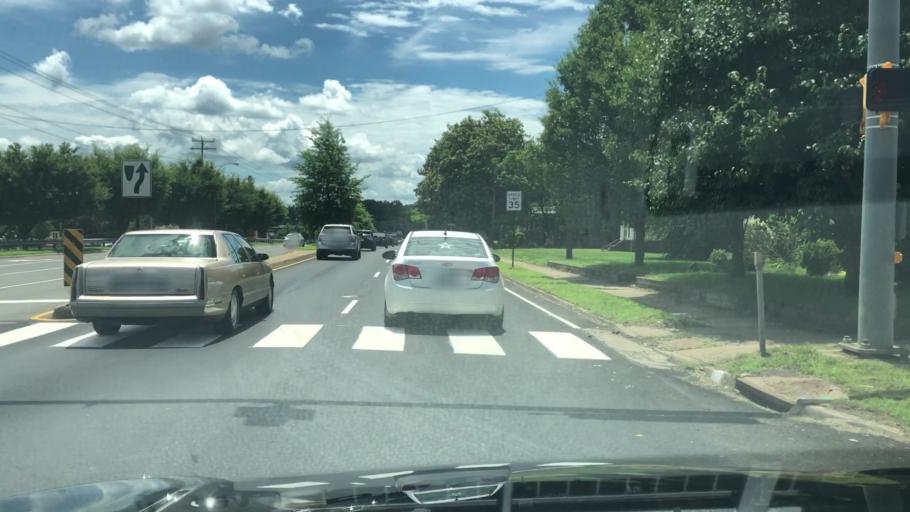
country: US
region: Virginia
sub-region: City of Fredericksburg
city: Fredericksburg
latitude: 38.2858
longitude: -77.4559
